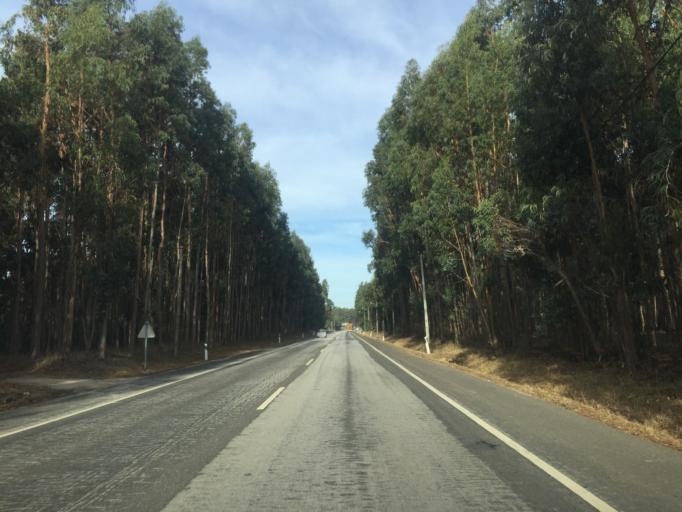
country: PT
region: Coimbra
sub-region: Figueira da Foz
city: Lavos
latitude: 40.0332
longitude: -8.8422
